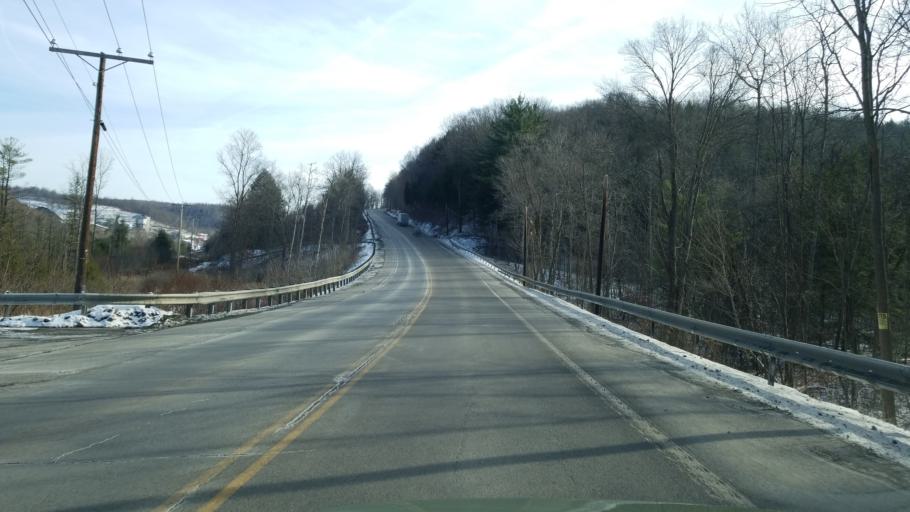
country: US
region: Pennsylvania
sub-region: Clearfield County
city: Treasure Lake
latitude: 41.2011
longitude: -78.5622
